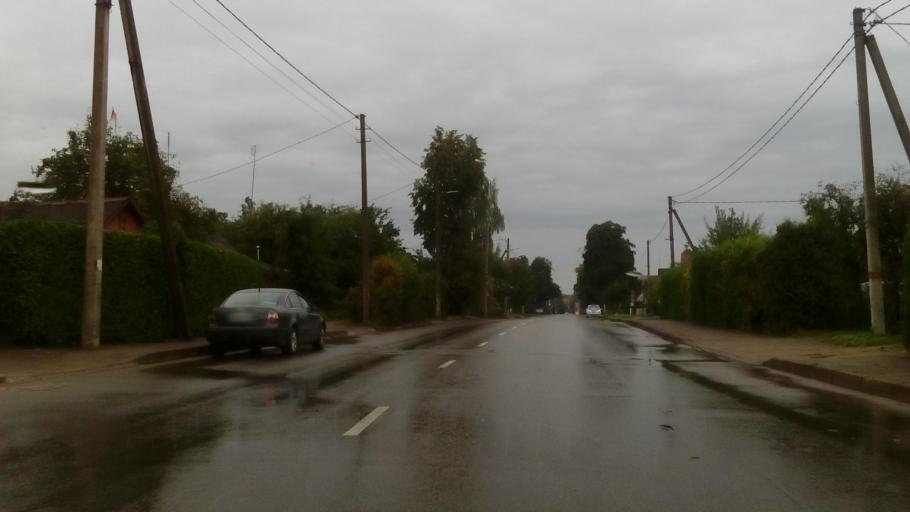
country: LT
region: Alytaus apskritis
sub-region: Alytus
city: Alytus
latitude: 54.3903
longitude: 24.0397
